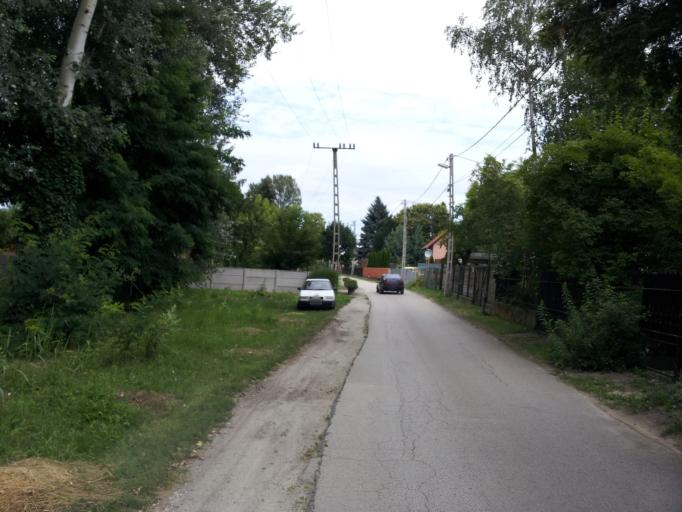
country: HU
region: Pest
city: Rackeve
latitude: 47.1736
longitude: 18.9517
